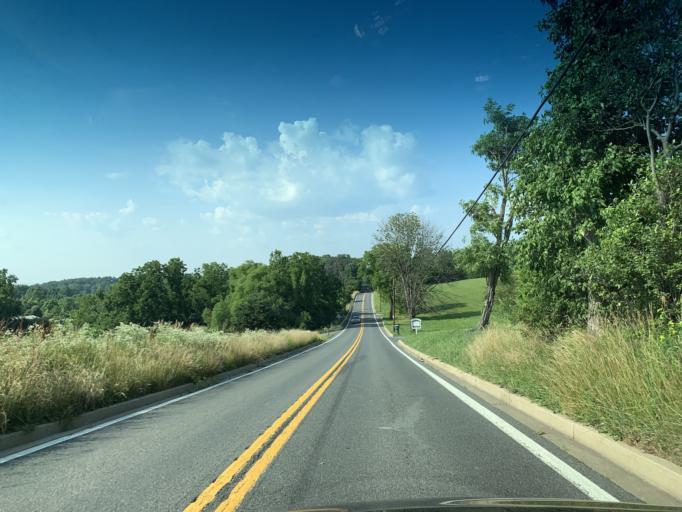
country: US
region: Maryland
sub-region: Montgomery County
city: Clarksburg
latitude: 39.2550
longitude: -77.3462
